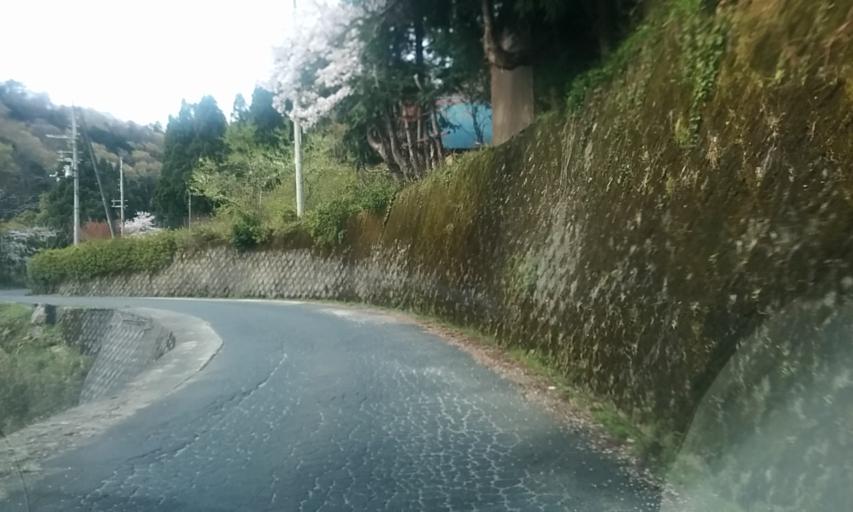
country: JP
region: Kyoto
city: Miyazu
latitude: 35.5869
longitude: 135.1781
